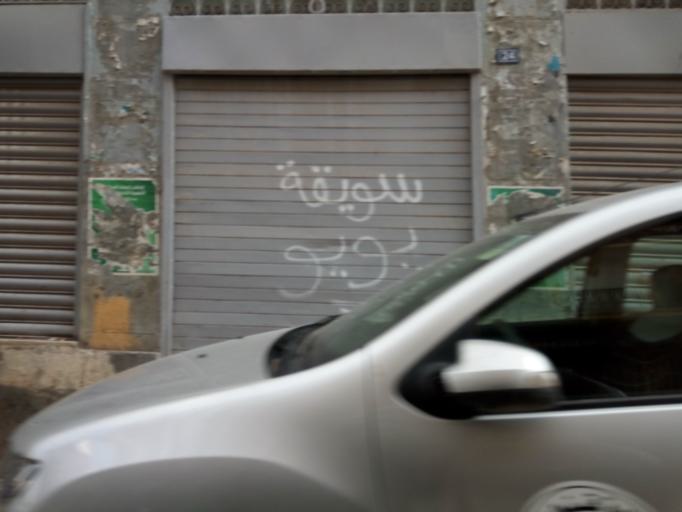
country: DZ
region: Constantine
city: Constantine
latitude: 36.3663
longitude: 6.6126
